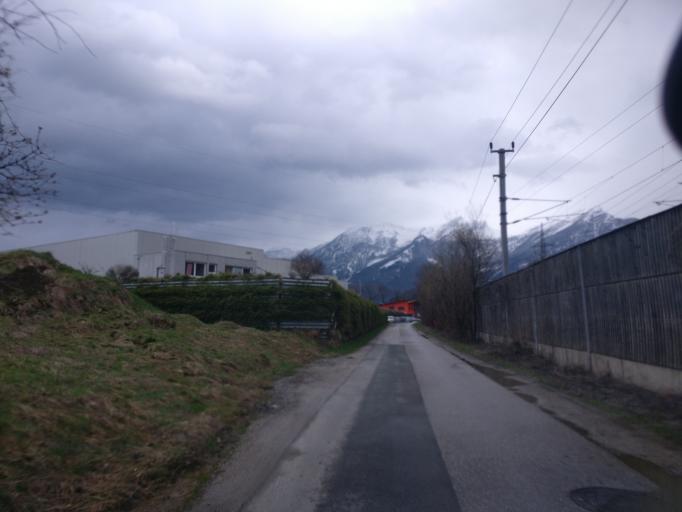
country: AT
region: Salzburg
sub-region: Politischer Bezirk Hallein
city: Golling an der Salzach
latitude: 47.6086
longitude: 13.1598
